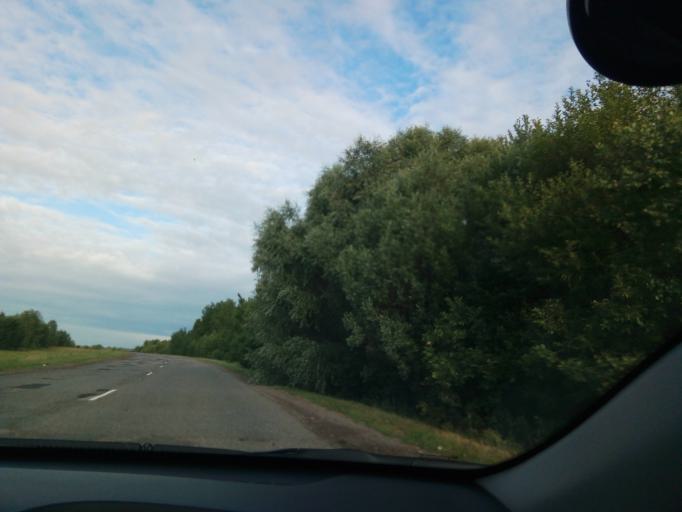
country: RU
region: Rjazan
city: Yermish'
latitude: 54.7844
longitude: 42.4339
